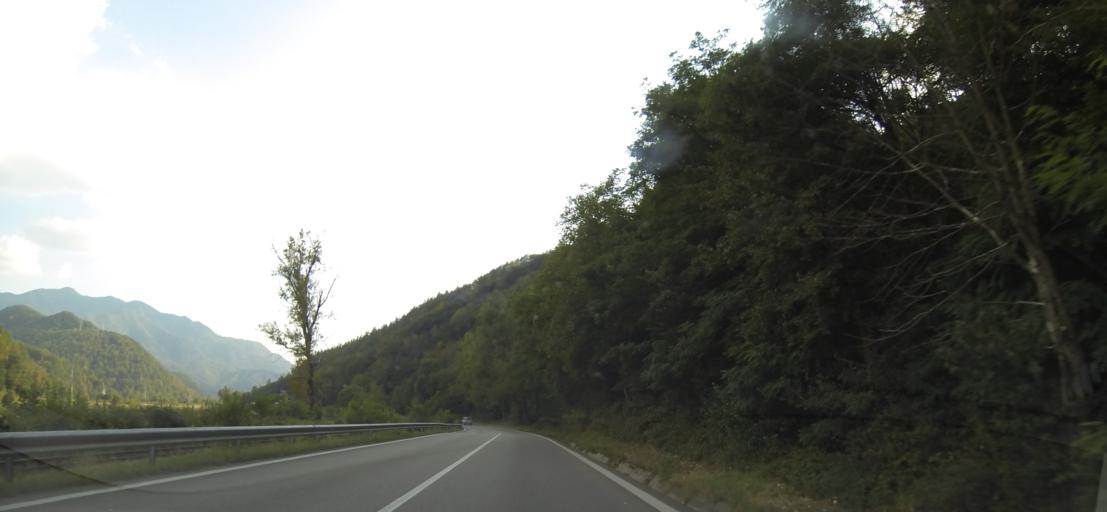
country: RO
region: Valcea
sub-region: Comuna Racovita
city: Racovita
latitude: 45.3834
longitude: 24.2949
